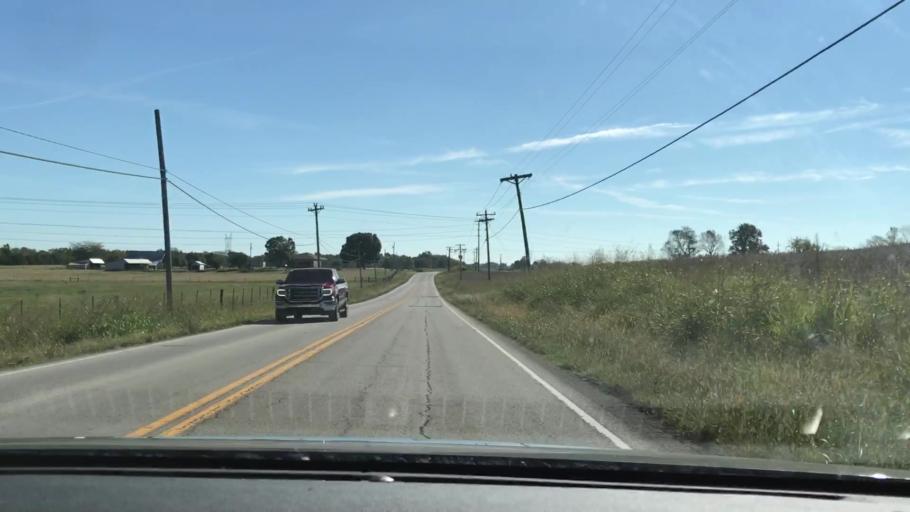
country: US
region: Kentucky
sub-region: Christian County
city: Hopkinsville
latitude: 36.8612
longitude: -87.4371
